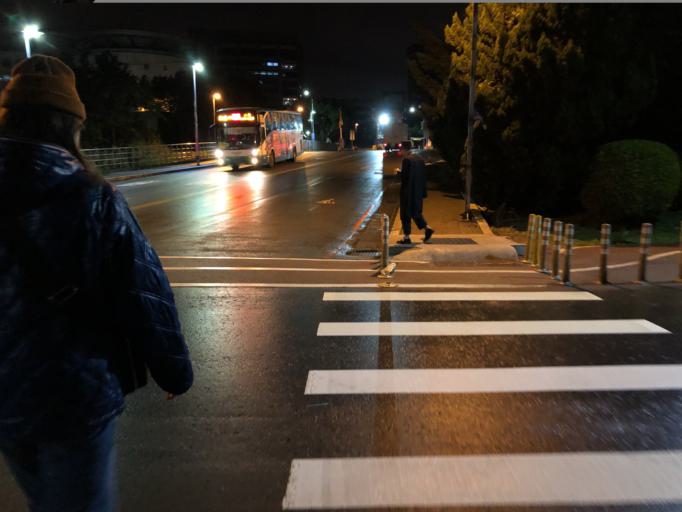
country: TW
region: Taiwan
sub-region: Taoyuan
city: Taoyuan
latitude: 25.0333
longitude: 121.3871
